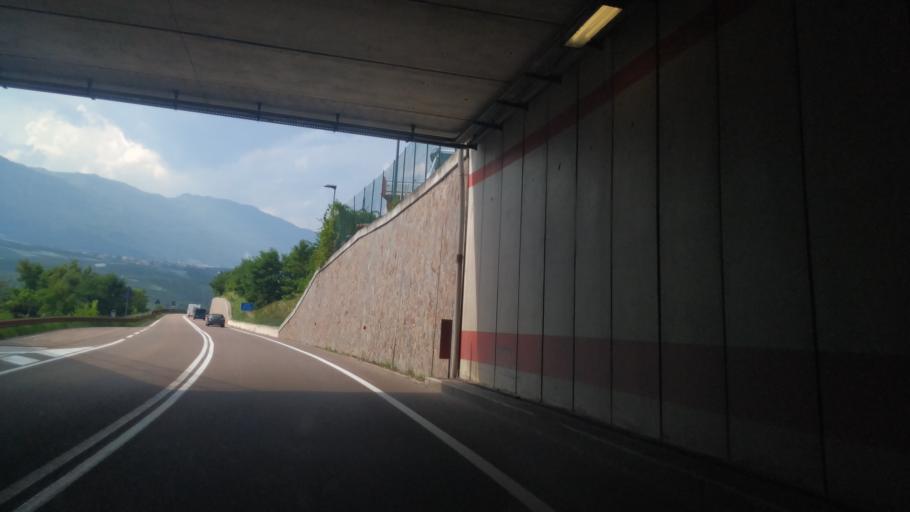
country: IT
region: Trentino-Alto Adige
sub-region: Provincia di Trento
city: Taio
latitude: 46.3128
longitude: 11.0698
